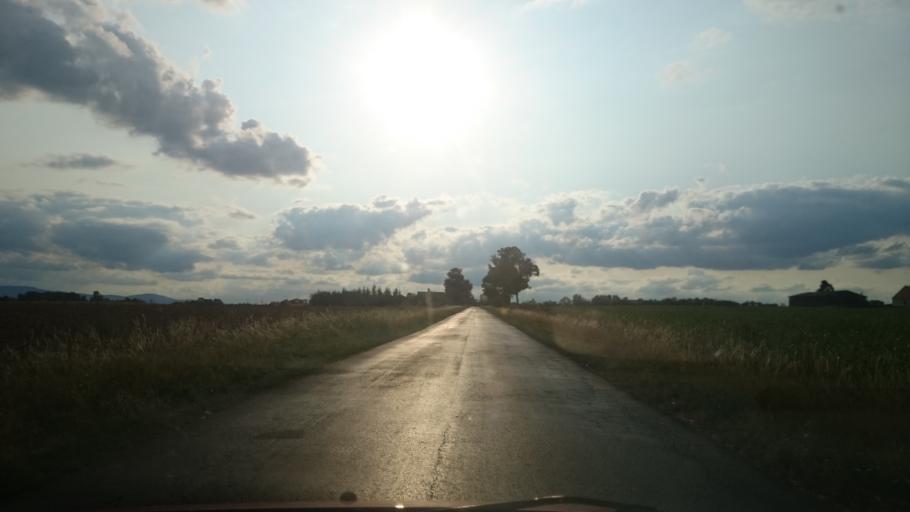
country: PL
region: Opole Voivodeship
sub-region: Powiat nyski
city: Otmuchow
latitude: 50.5064
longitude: 17.1724
